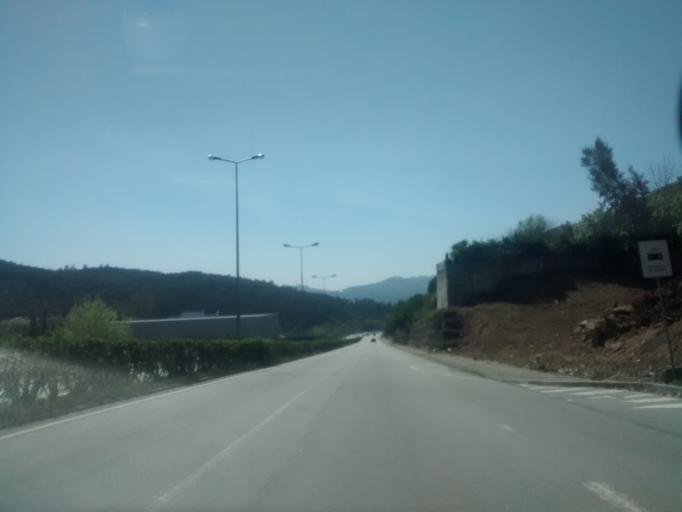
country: PT
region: Braga
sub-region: Braga
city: Braga
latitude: 41.5303
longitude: -8.4129
